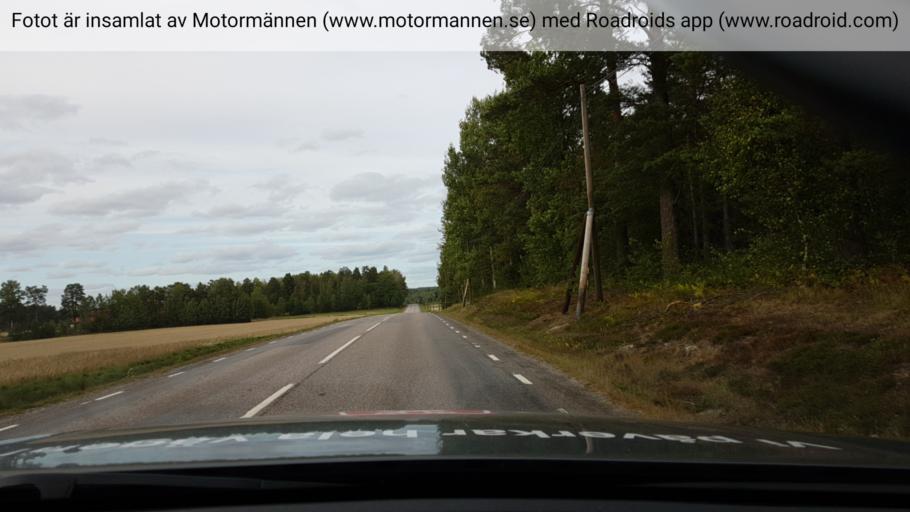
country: SE
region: Stockholm
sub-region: Haninge Kommun
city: Haninge
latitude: 59.0953
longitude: 18.1798
